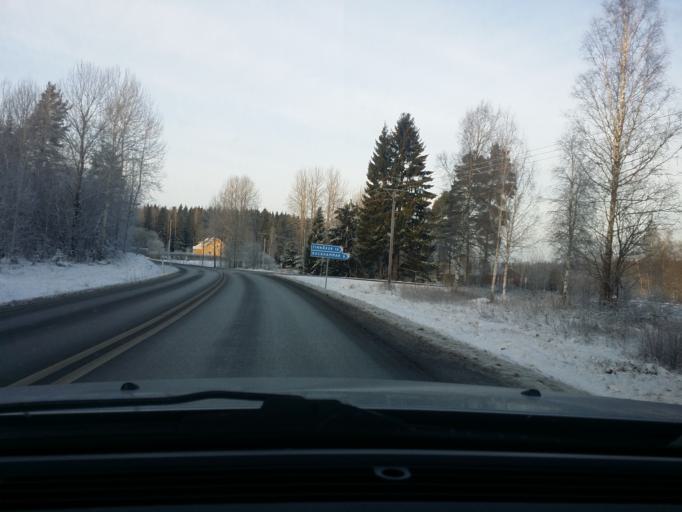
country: SE
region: OErebro
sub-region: Lindesbergs Kommun
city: Frovi
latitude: 59.5058
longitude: 15.3720
